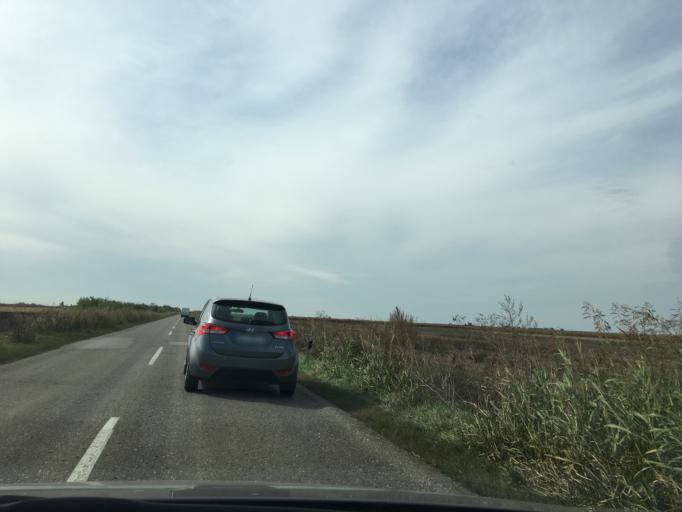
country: RS
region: Autonomna Pokrajina Vojvodina
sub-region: Juznobacki Okrug
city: Temerin
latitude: 45.4791
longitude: 19.9264
